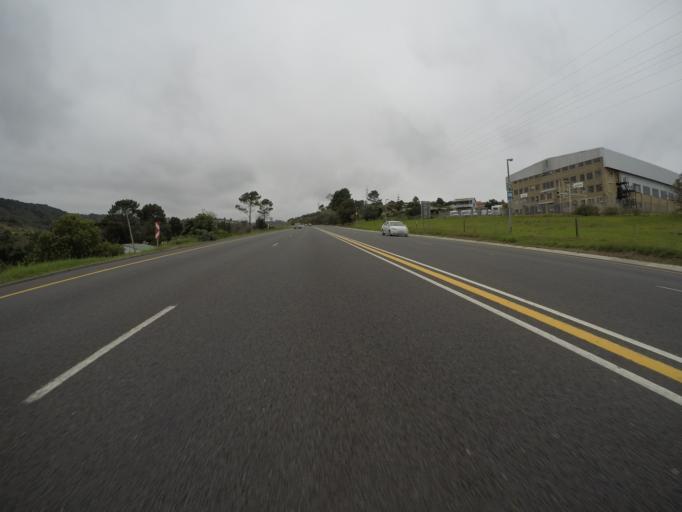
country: ZA
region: Western Cape
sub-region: Eden District Municipality
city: Knysna
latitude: -34.0434
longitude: 23.0844
